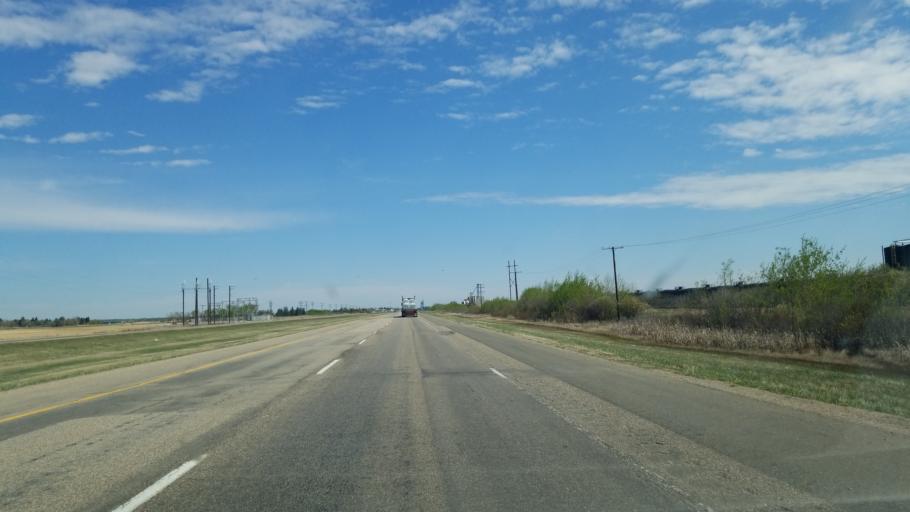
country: CA
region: Saskatchewan
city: Lloydminster
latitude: 53.1401
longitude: -109.6557
